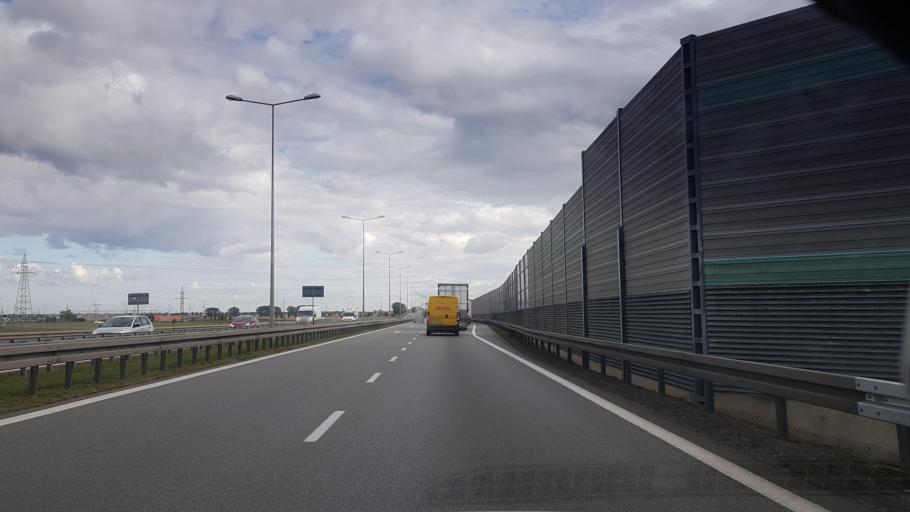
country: PL
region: Greater Poland Voivodeship
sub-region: Powiat poznanski
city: Komorniki
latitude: 52.3475
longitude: 16.7616
